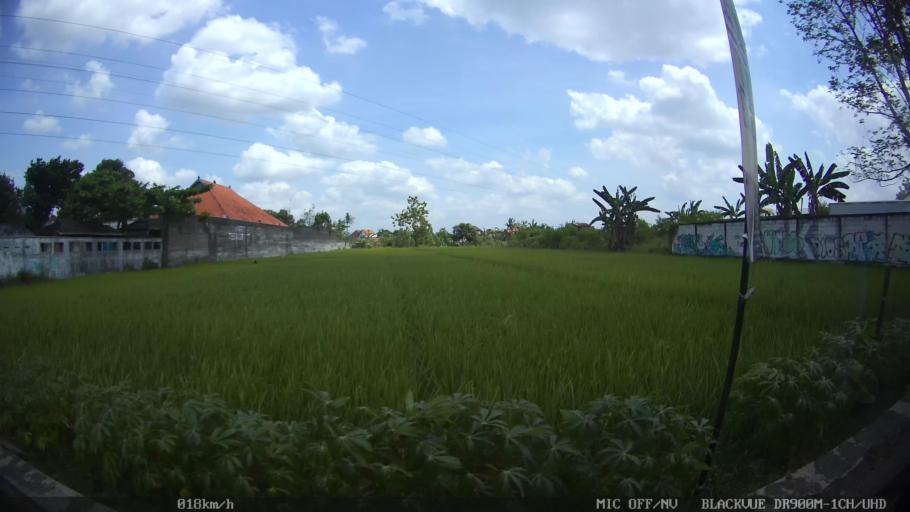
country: ID
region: Daerah Istimewa Yogyakarta
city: Kasihan
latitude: -7.8236
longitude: 110.3474
